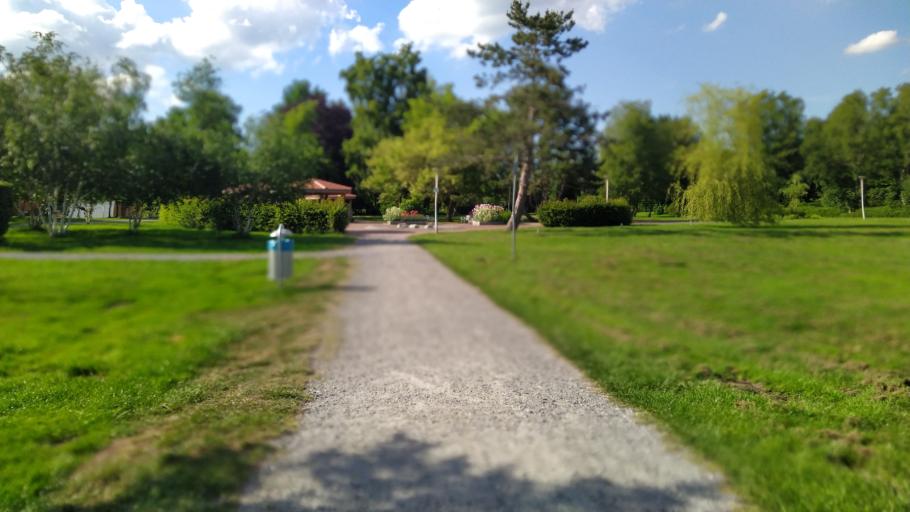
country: DE
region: Lower Saxony
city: Lintig
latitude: 53.6280
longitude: 8.8419
